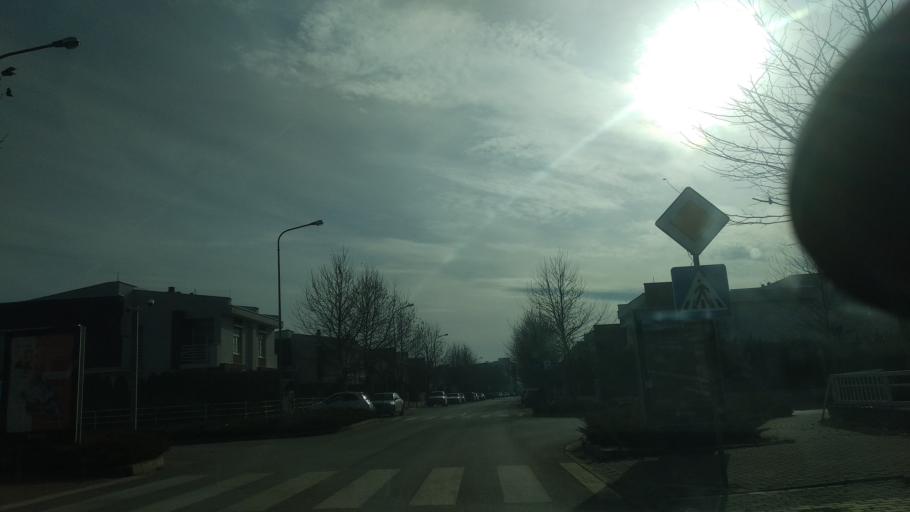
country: XK
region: Pristina
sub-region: Komuna e Gracanices
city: Glanica
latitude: 42.5882
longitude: 21.1078
